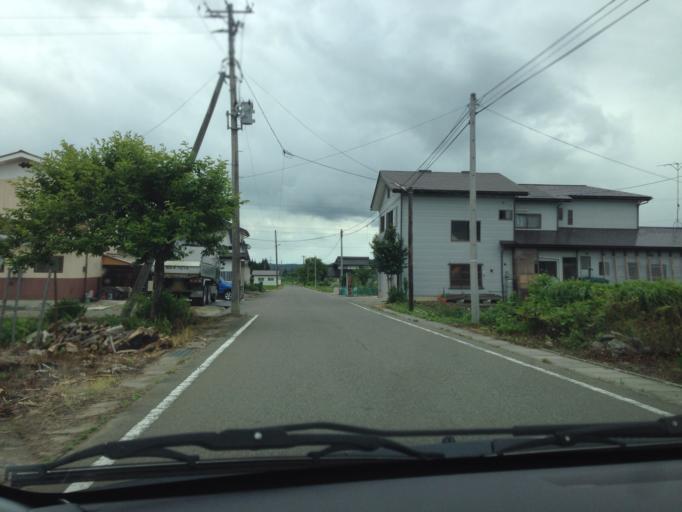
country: JP
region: Fukushima
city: Kitakata
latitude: 37.7115
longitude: 139.8757
